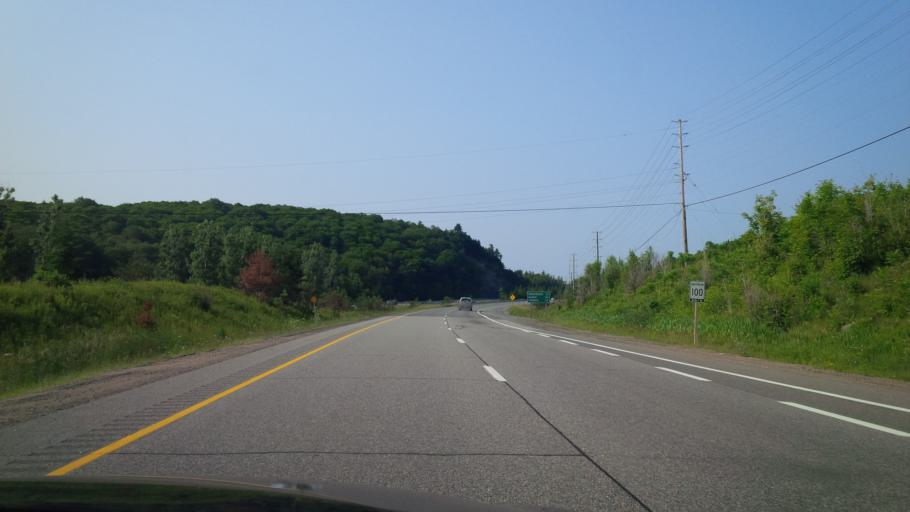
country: CA
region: Ontario
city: Huntsville
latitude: 45.3098
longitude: -79.2461
